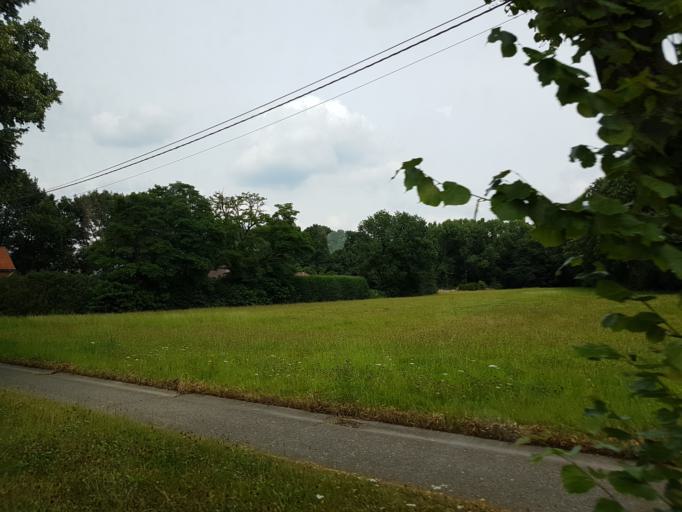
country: BE
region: Flanders
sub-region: Provincie Antwerpen
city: Olen
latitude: 51.1375
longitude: 4.8629
